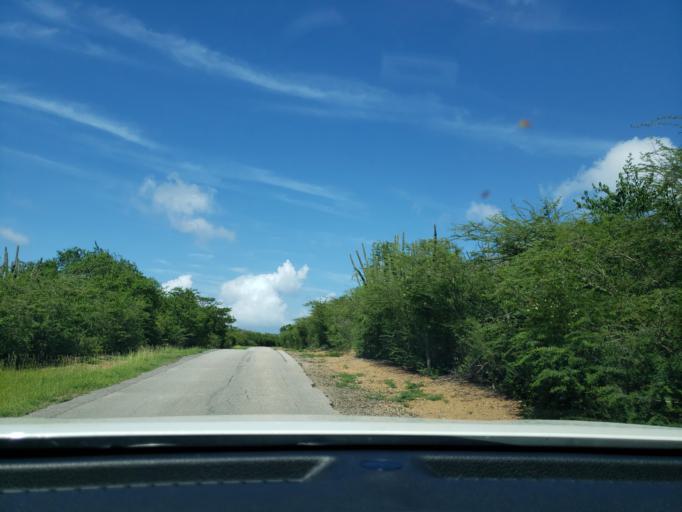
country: CW
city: Dorp Soto
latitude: 12.3458
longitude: -69.1531
